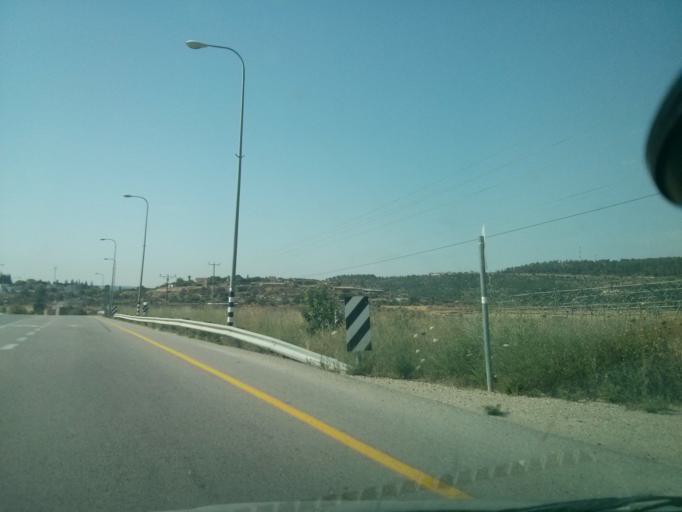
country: IL
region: Jerusalem
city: Bet Shemesh
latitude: 31.6824
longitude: 35.0027
